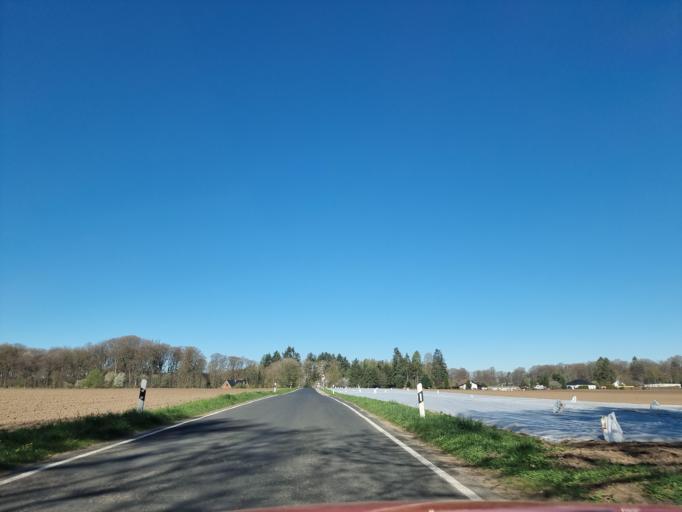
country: DE
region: Rheinland-Pfalz
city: Prumzurlay
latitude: 49.8680
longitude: 6.4491
